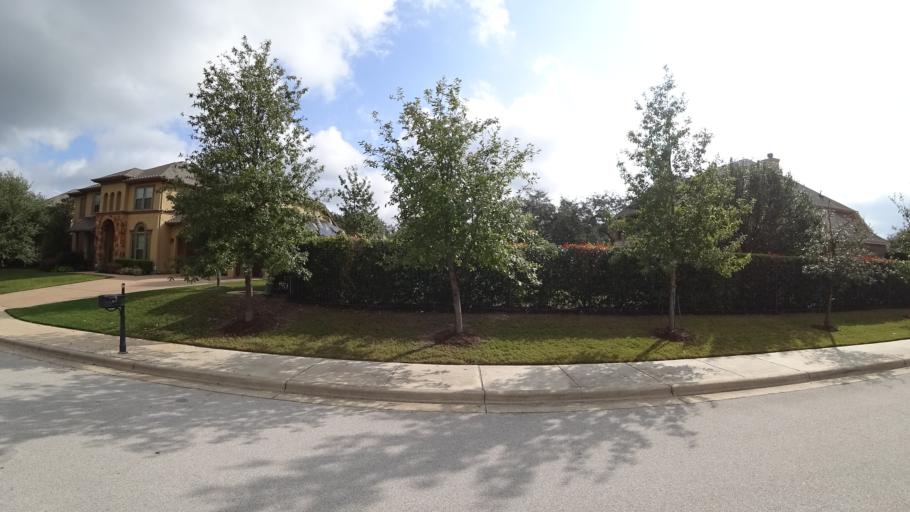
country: US
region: Texas
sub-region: Travis County
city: Barton Creek
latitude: 30.3131
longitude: -97.8999
